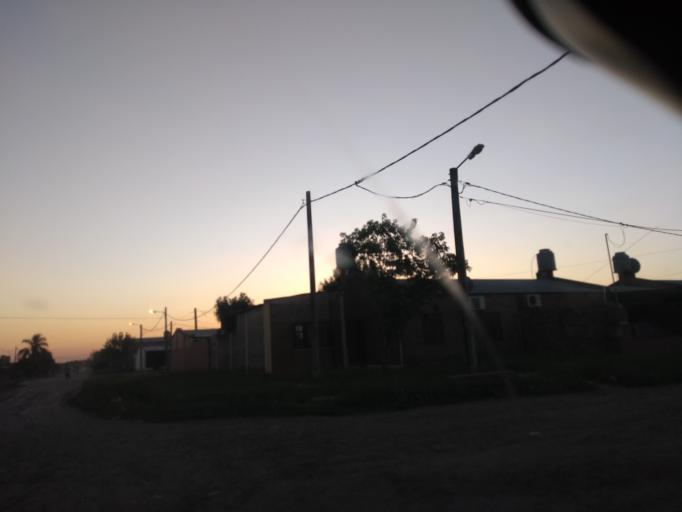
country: AR
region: Chaco
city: Fontana
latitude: -27.4171
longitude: -59.0452
